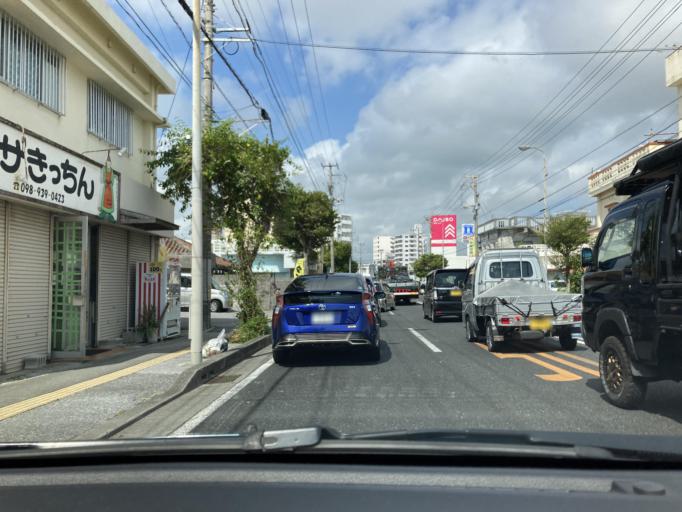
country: JP
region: Okinawa
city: Okinawa
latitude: 26.3337
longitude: 127.8195
